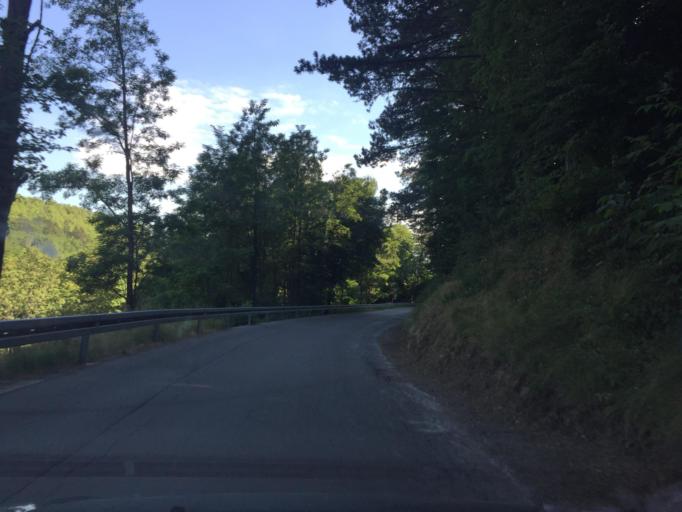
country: HR
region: Primorsko-Goranska
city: Klana
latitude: 45.4553
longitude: 14.3783
